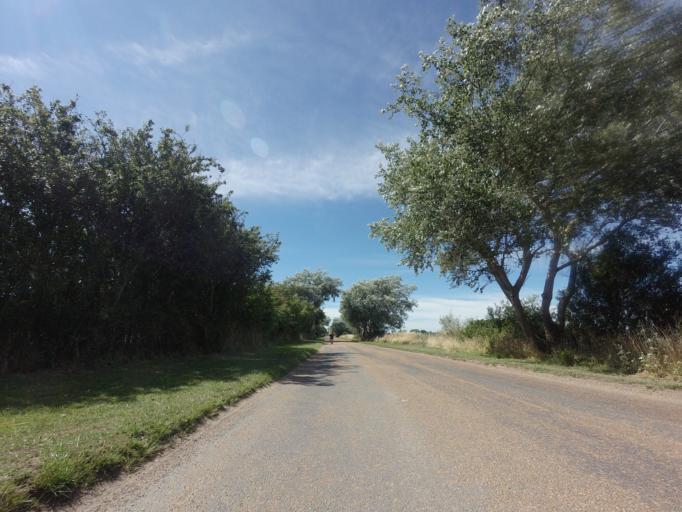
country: GB
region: England
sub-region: Kent
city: Sandwich
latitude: 51.2684
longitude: 1.3754
